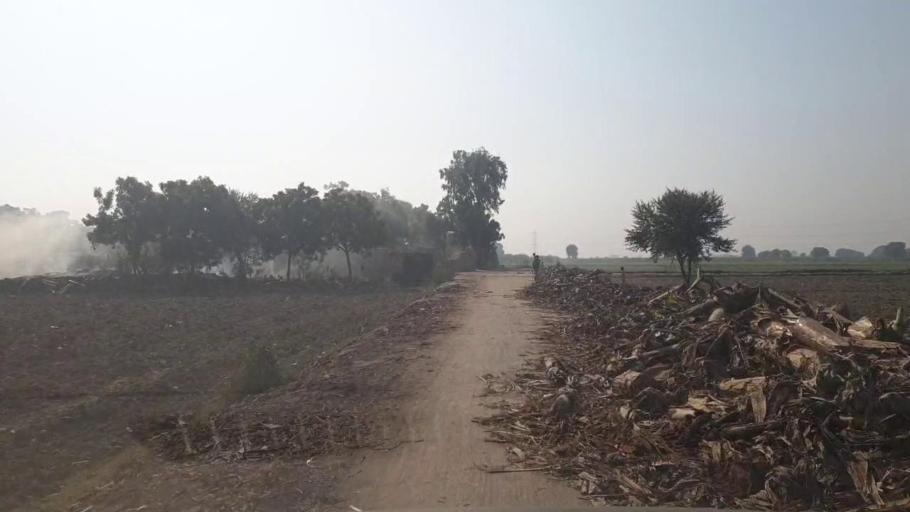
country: PK
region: Sindh
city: Tando Allahyar
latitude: 25.4641
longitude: 68.7633
